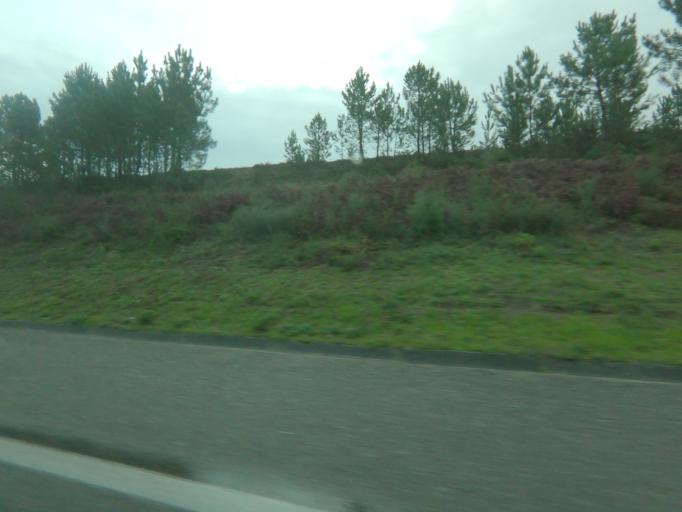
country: PT
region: Viana do Castelo
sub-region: Valenca
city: Valenza
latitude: 41.9814
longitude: -8.6507
